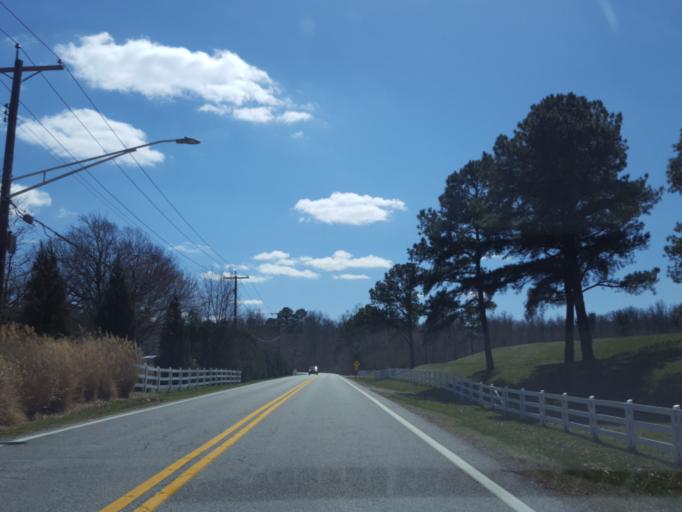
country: US
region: Maryland
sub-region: Calvert County
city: North Beach
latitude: 38.7248
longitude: -76.5445
